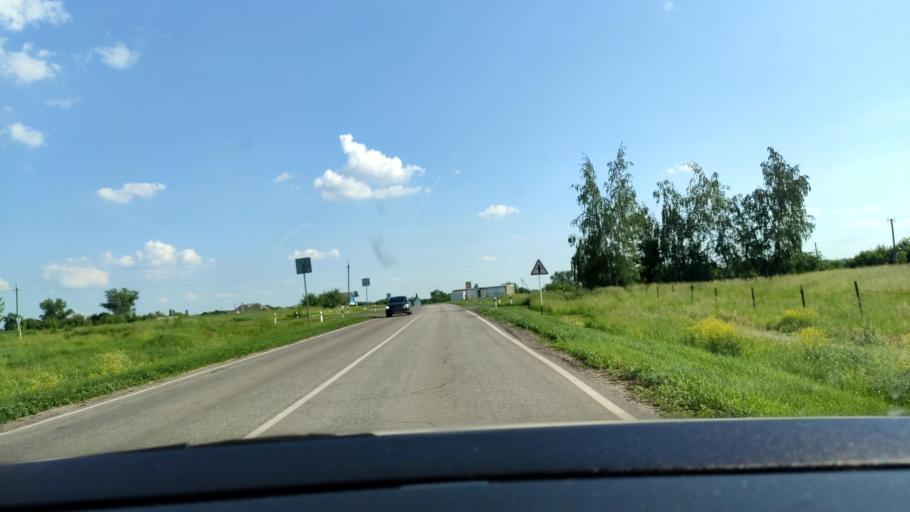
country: RU
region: Voronezj
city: Verkhnyaya Khava
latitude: 51.6768
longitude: 39.9416
